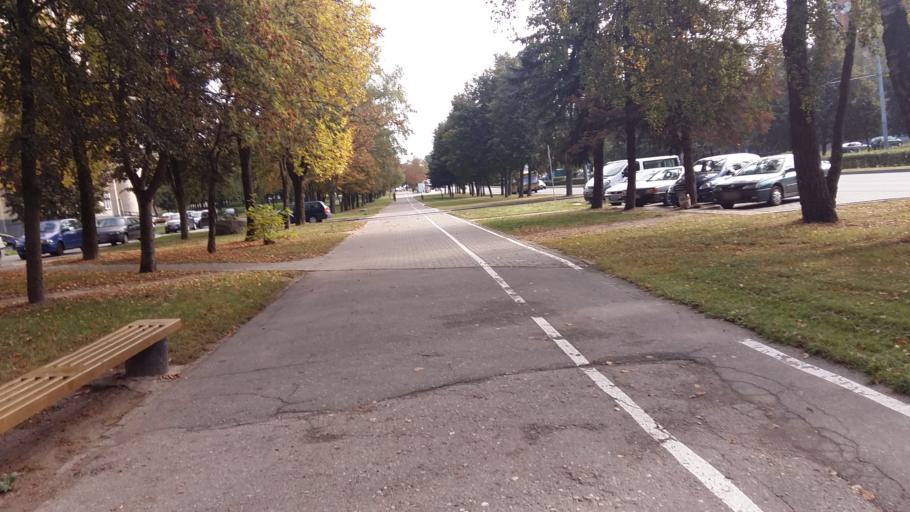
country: BY
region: Grodnenskaya
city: Hrodna
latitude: 53.6991
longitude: 23.8142
